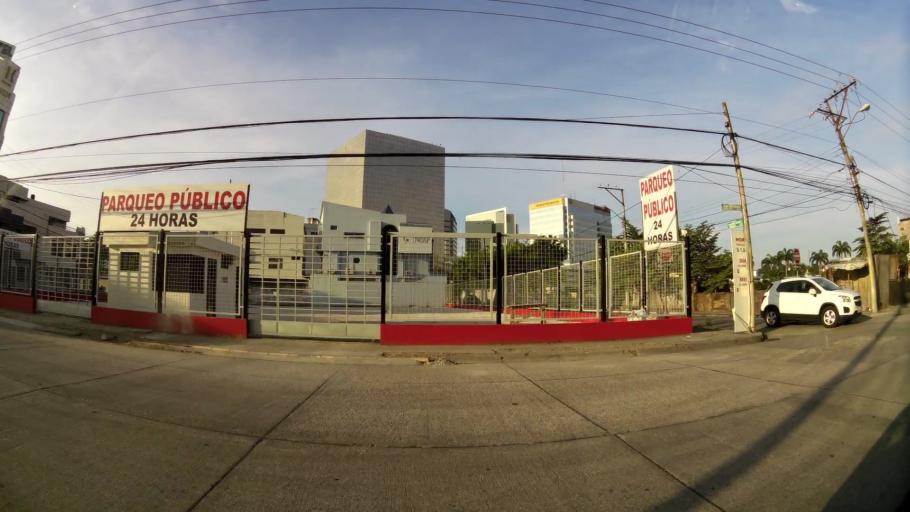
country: EC
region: Guayas
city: Eloy Alfaro
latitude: -2.1602
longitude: -79.8978
